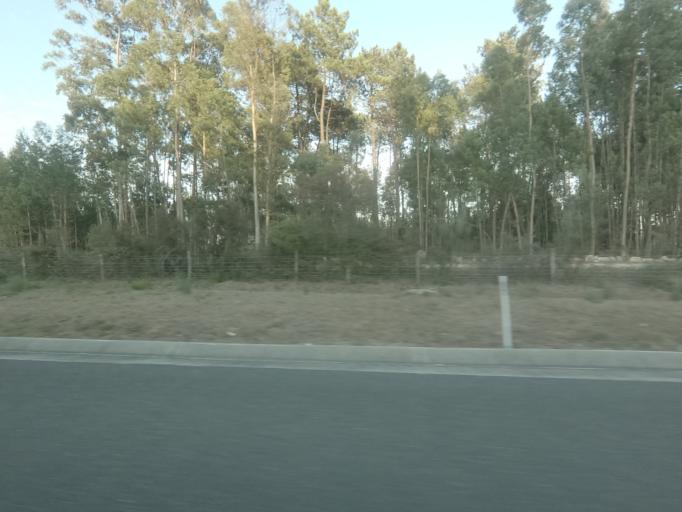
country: PT
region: Leiria
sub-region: Leiria
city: Santa Catarina da Serra
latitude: 39.6544
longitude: -8.6960
